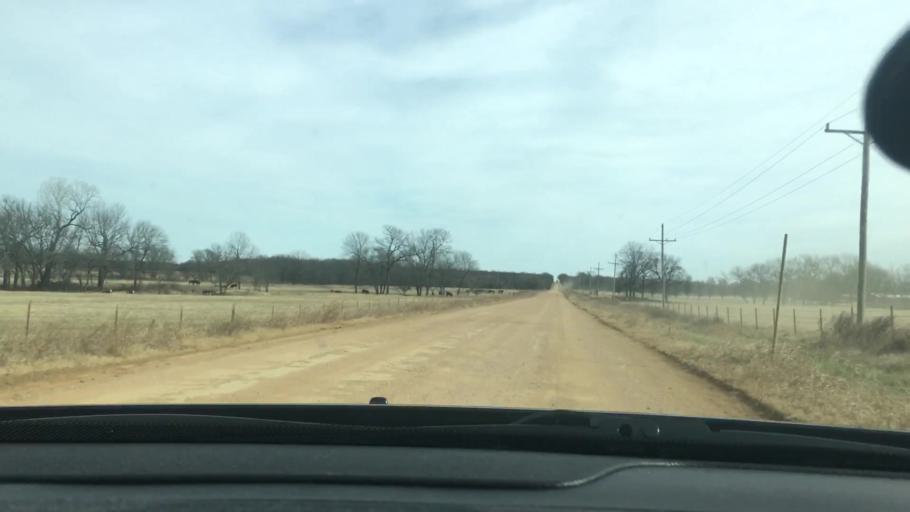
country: US
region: Oklahoma
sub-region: Murray County
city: Sulphur
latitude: 34.4049
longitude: -96.9152
